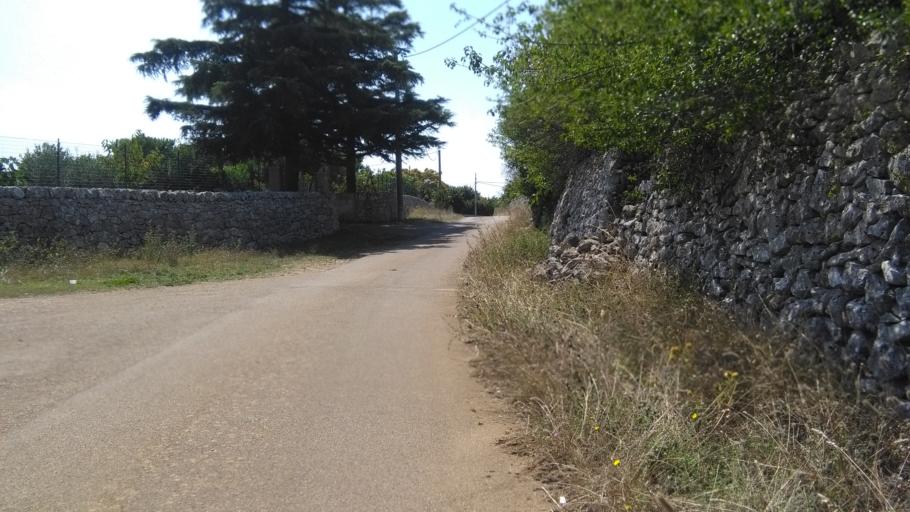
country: IT
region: Apulia
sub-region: Provincia di Bari
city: Noci
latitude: 40.8234
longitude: 17.1397
